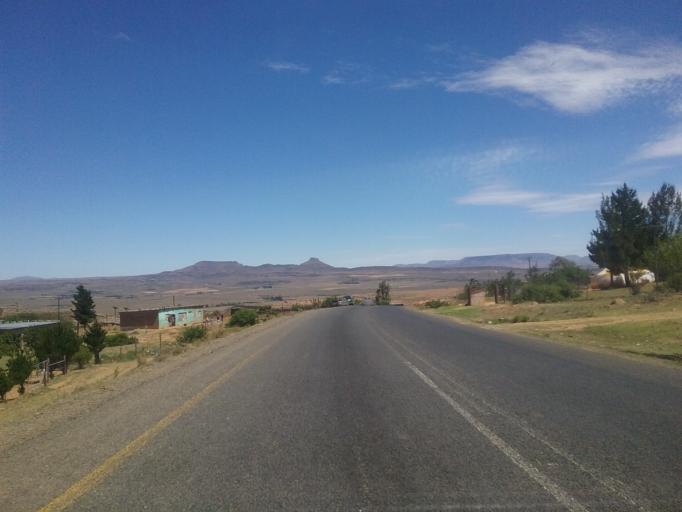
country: LS
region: Mohale's Hoek District
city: Mohale's Hoek
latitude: -30.2015
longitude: 27.4188
